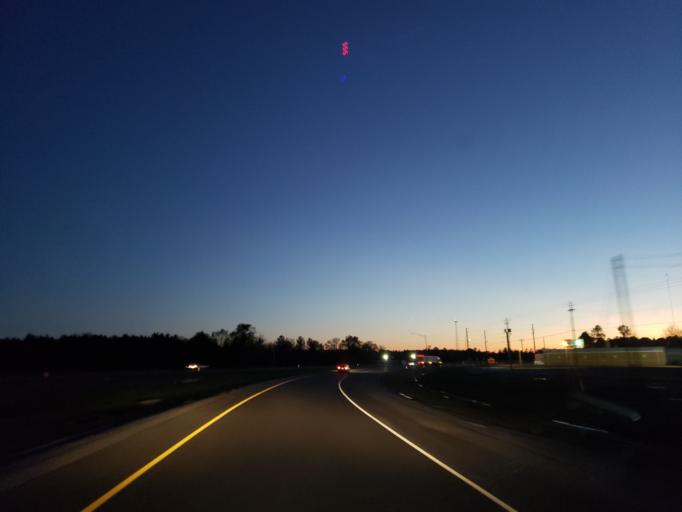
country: US
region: Mississippi
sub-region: Forrest County
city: Glendale
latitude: 31.3796
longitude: -89.3271
